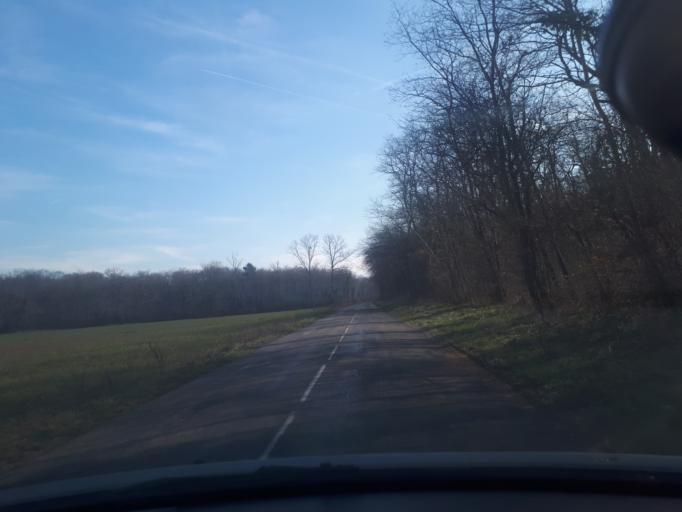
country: FR
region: Rhone-Alpes
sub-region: Departement de l'Isere
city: Salagnon
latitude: 45.6705
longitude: 5.3825
